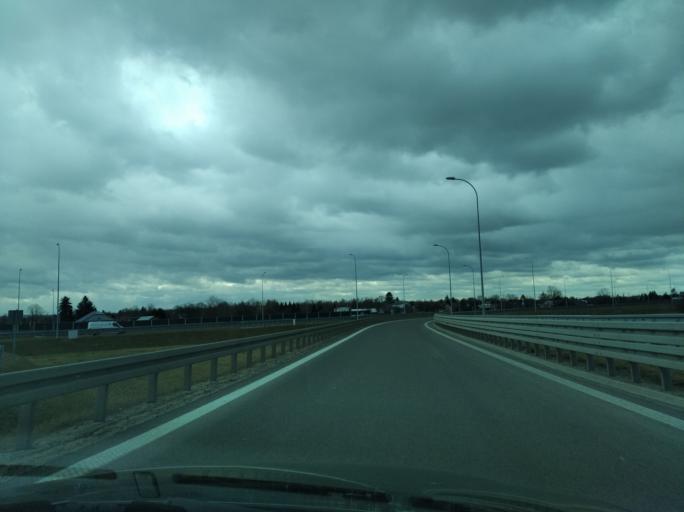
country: PL
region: Subcarpathian Voivodeship
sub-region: Powiat lancucki
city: Lancut
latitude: 50.1003
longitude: 22.2224
